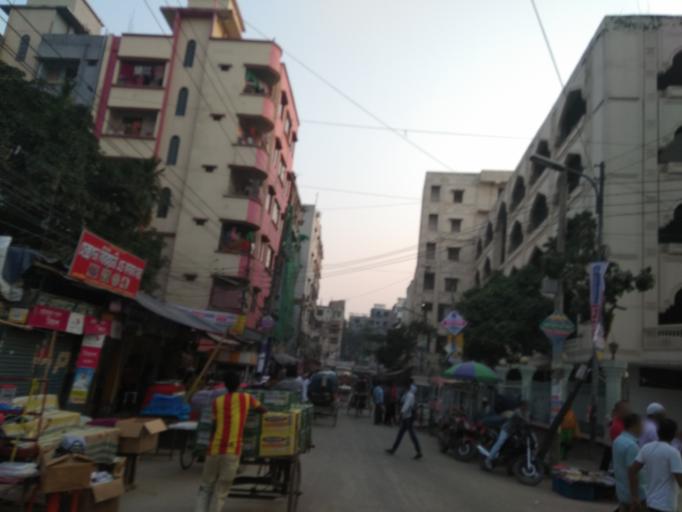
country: BD
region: Dhaka
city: Azimpur
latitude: 23.8112
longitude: 90.3641
